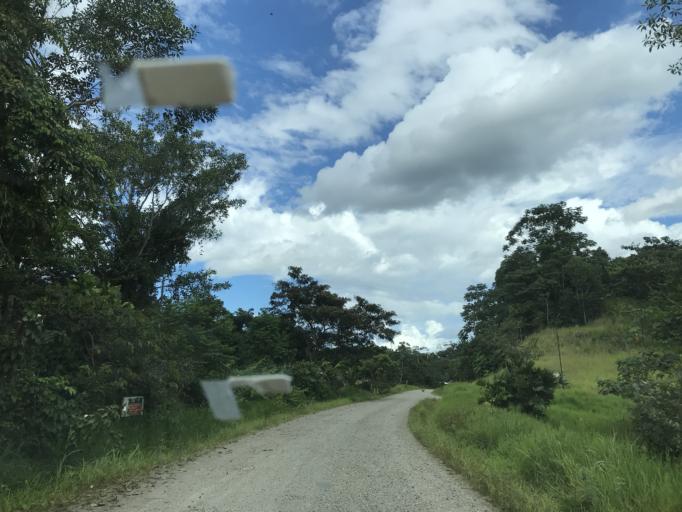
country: EC
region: Orellana
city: Puerto Francisco de Orellana
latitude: -0.6095
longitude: -76.4672
